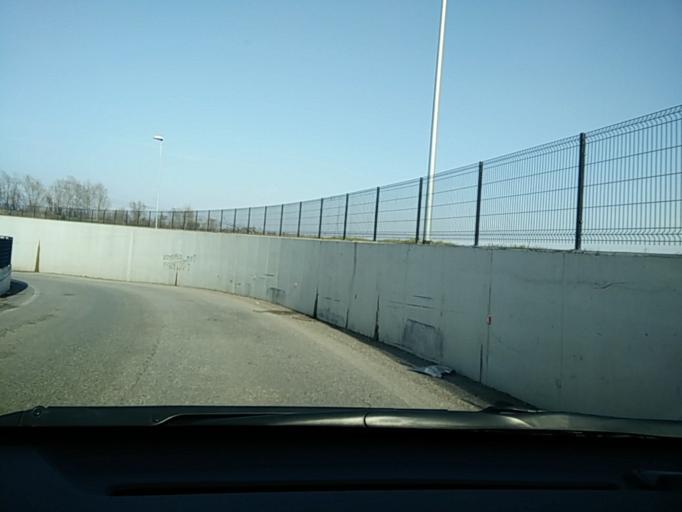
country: IT
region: Veneto
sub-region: Provincia di Venezia
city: Fossalta di Piave
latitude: 45.6243
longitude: 12.5040
